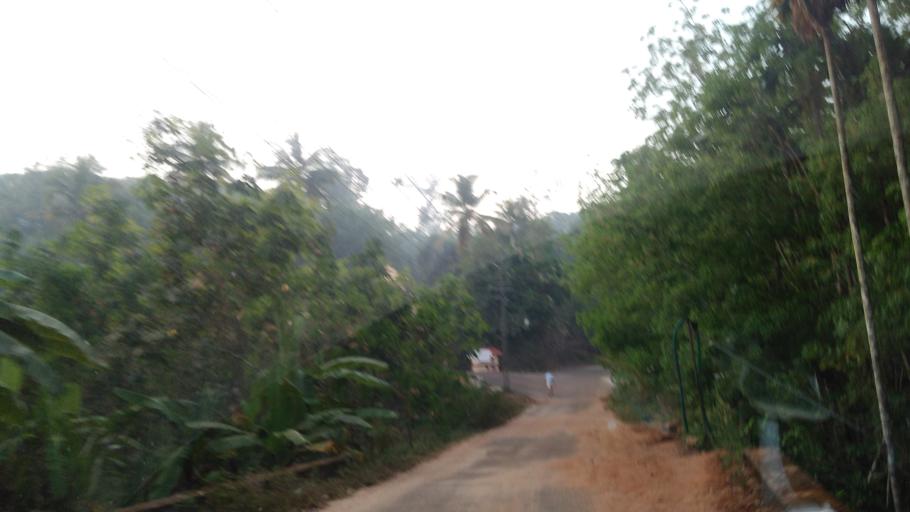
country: IN
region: Kerala
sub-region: Kottayam
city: Palackattumala
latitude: 9.8484
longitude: 76.6530
